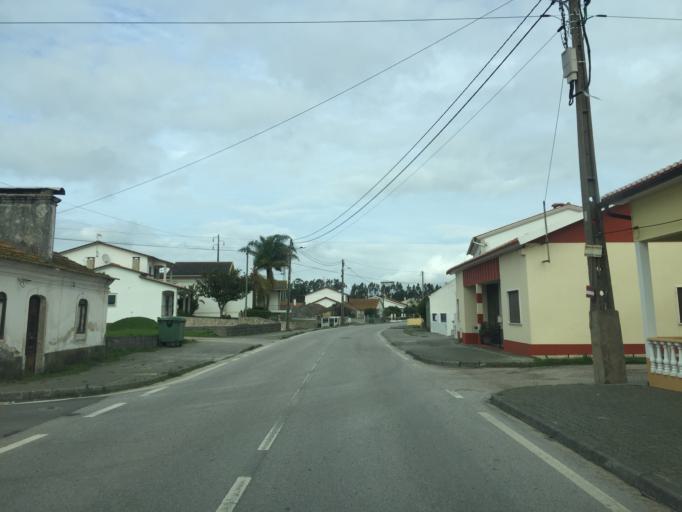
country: PT
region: Coimbra
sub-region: Figueira da Foz
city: Lavos
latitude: 40.0376
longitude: -8.8201
